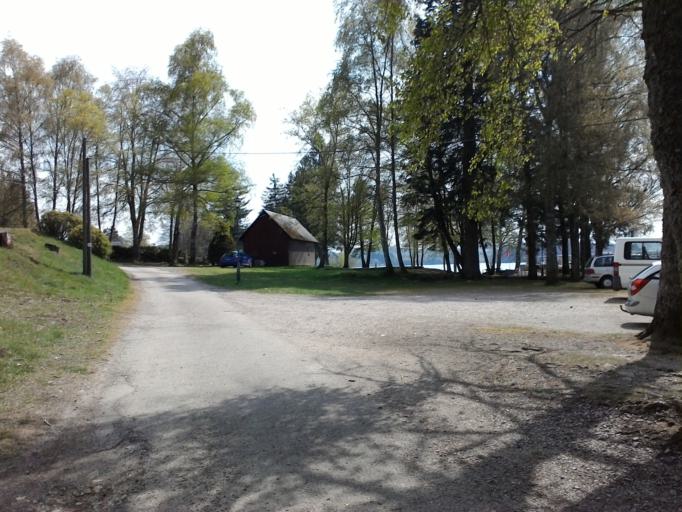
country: FR
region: Bourgogne
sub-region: Departement de la Nievre
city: Chateau-Chinon(Ville)
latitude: 47.1882
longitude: 4.0690
